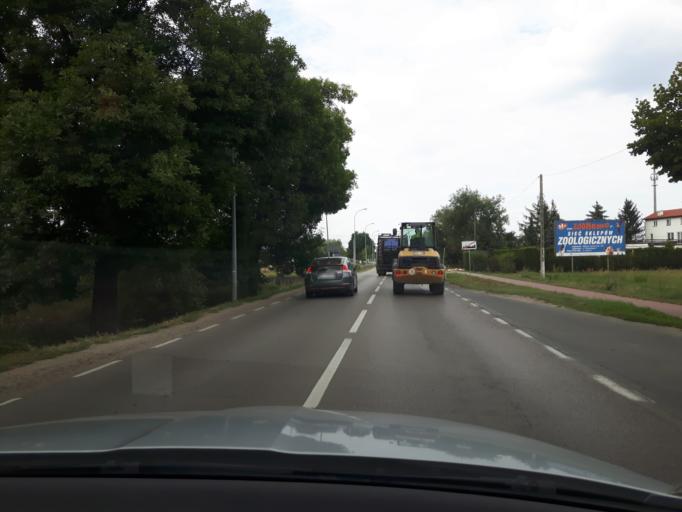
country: PL
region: Masovian Voivodeship
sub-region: Powiat legionowski
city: Stanislawow Pierwszy
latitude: 52.3656
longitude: 21.0284
